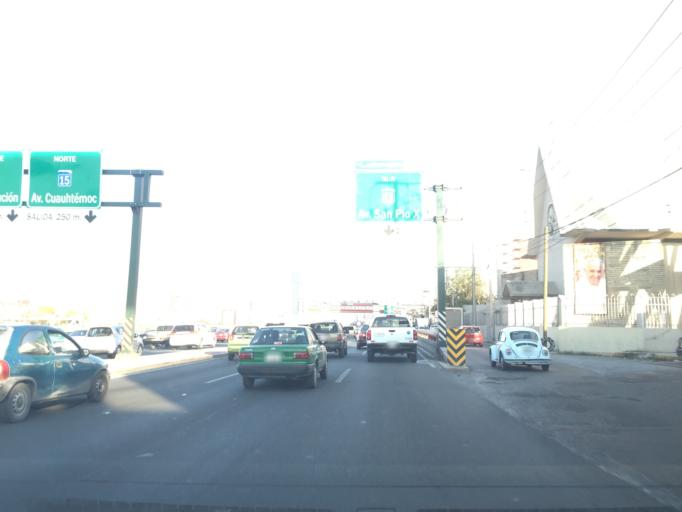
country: MX
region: Nuevo Leon
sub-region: Monterrey
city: Monterrey
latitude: 25.6656
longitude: -100.3330
